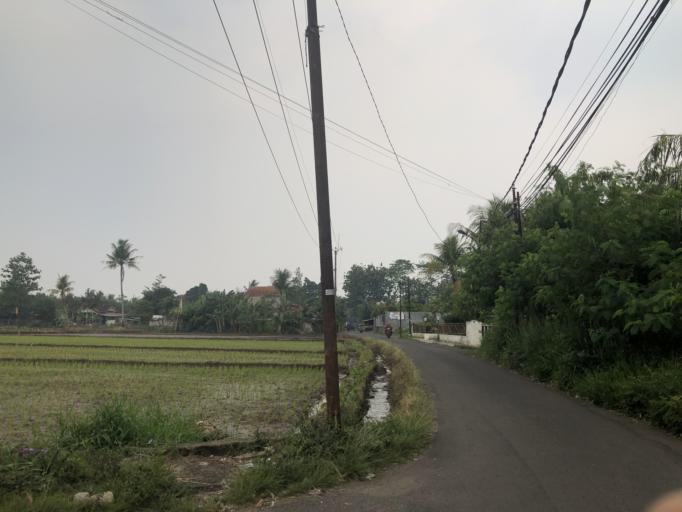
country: ID
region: West Java
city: Ciampea
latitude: -6.5673
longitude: 106.7458
